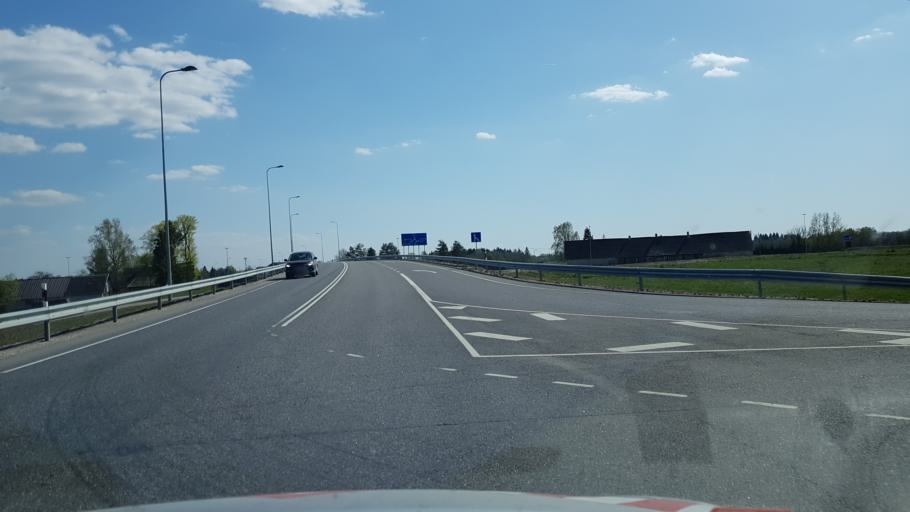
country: EE
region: Harju
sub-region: Raasiku vald
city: Arukula
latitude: 59.1851
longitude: 25.1160
